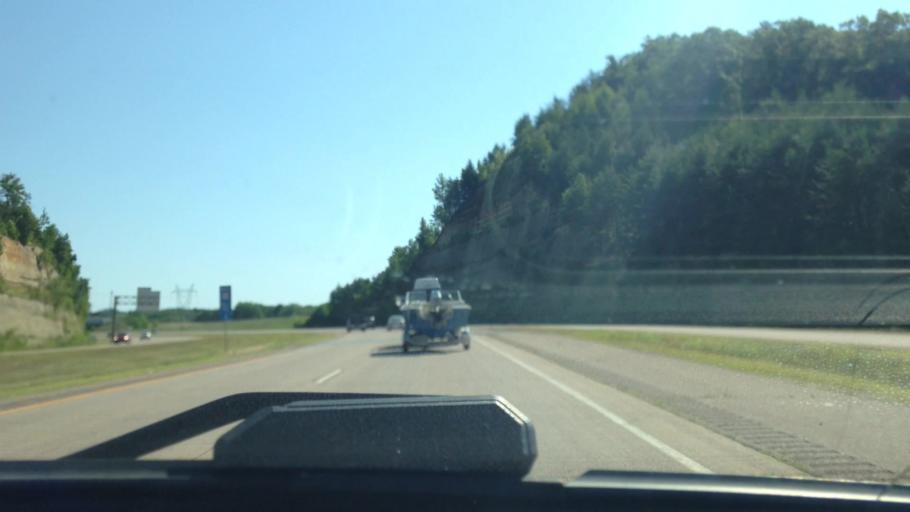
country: US
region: Wisconsin
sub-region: Eau Claire County
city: Seymour
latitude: 44.8366
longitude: -91.4461
